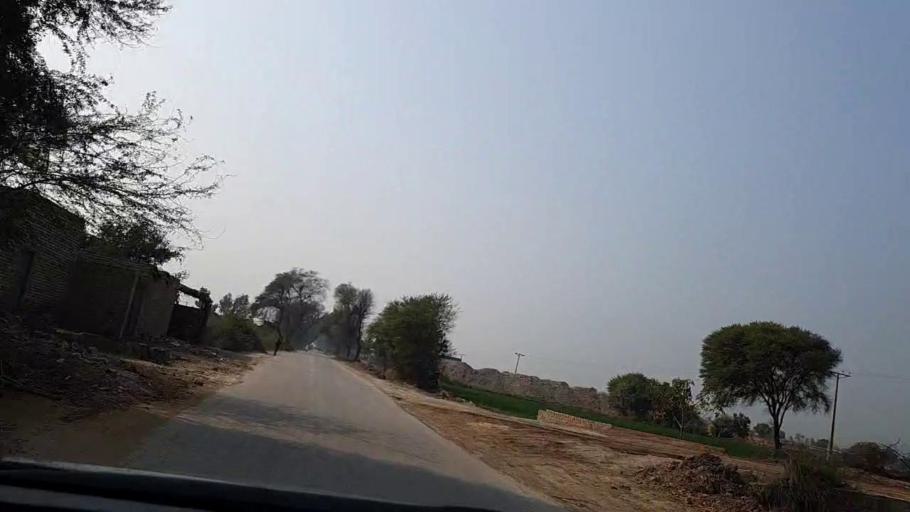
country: PK
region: Sindh
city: Sakrand
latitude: 26.1320
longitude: 68.2255
